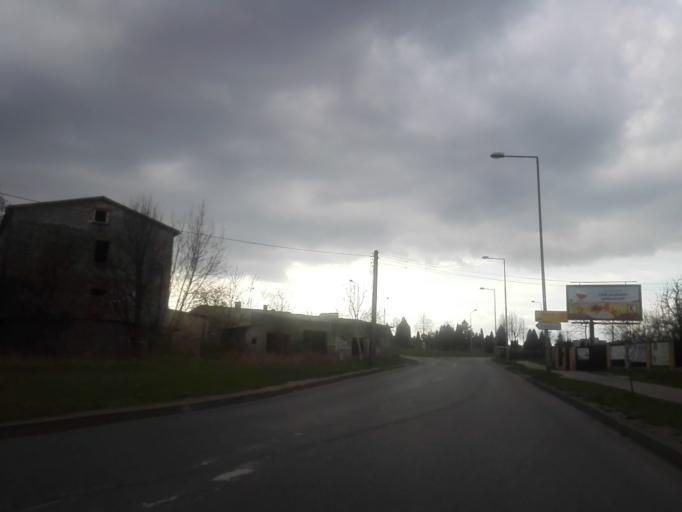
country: PL
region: Silesian Voivodeship
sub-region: Czestochowa
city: Czestochowa
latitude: 50.8291
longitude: 19.1376
